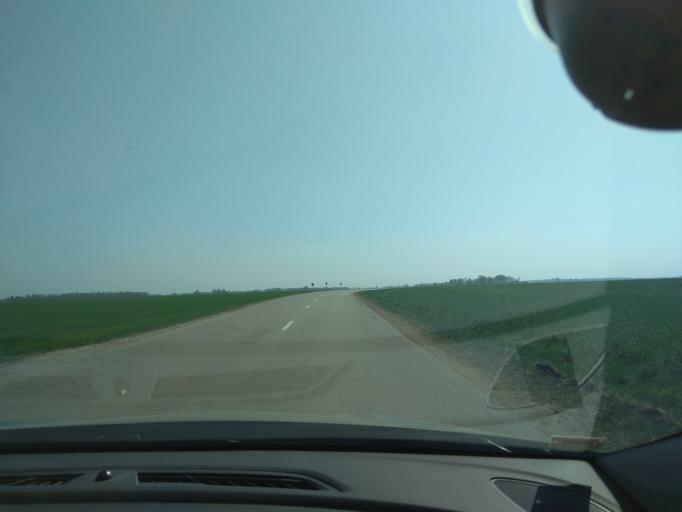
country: LT
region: Panevezys
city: Pasvalys
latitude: 55.9590
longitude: 24.2109
